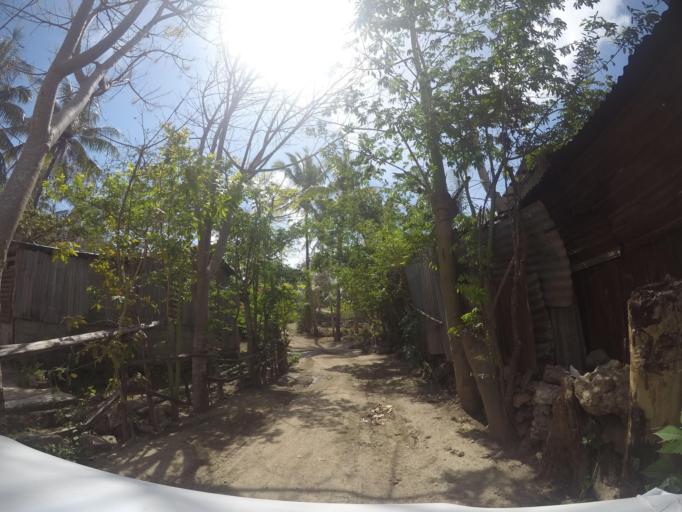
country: TL
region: Baucau
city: Baucau
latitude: -8.4670
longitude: 126.4614
